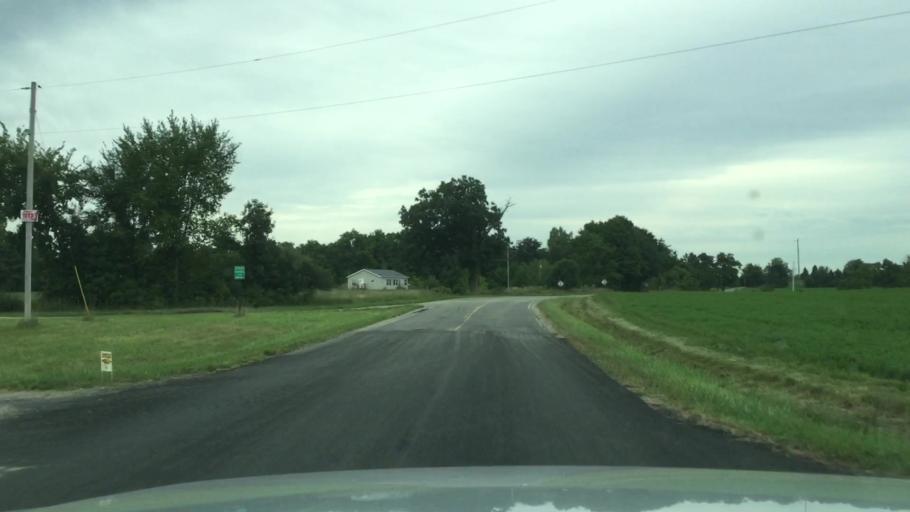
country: US
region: Michigan
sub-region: Shiawassee County
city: Durand
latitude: 42.8626
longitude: -84.0439
